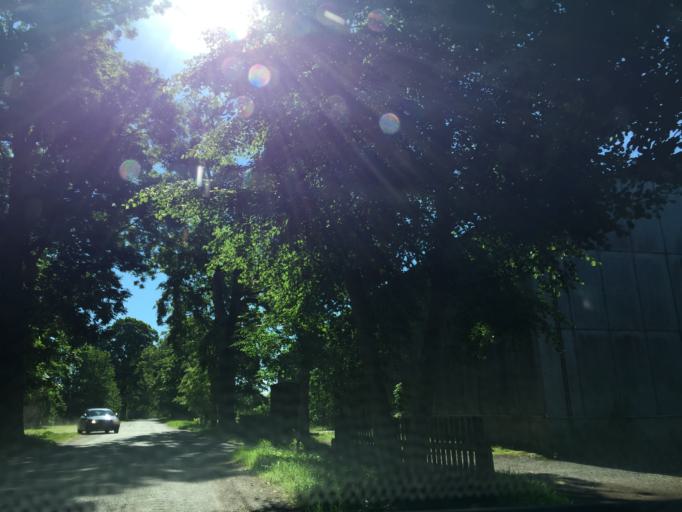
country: LV
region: Kuldigas Rajons
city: Kuldiga
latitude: 57.3268
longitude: 22.0175
